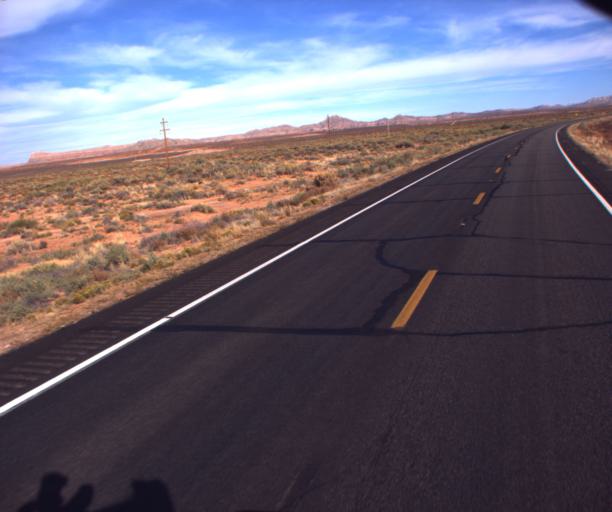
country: US
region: Arizona
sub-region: Apache County
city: Many Farms
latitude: 36.9416
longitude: -109.6503
